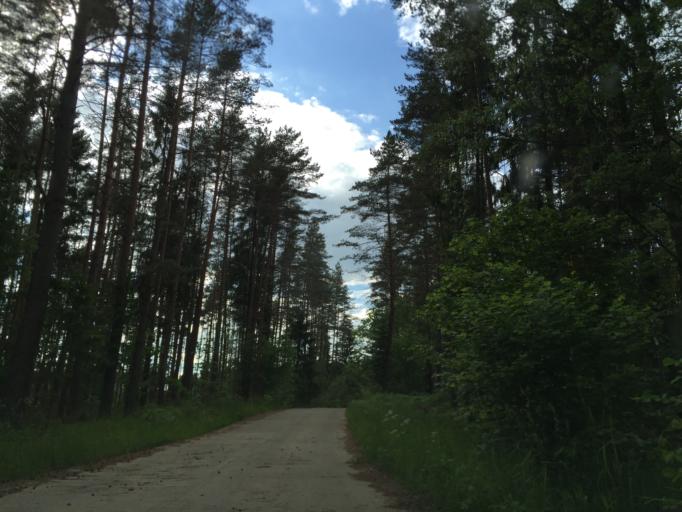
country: LV
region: Dobeles Rajons
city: Dobele
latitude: 56.6486
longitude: 23.1867
